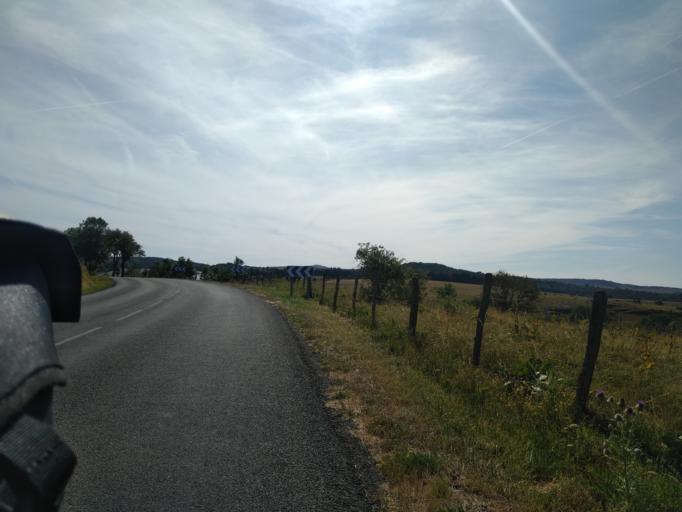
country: FR
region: Auvergne
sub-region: Departement du Cantal
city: Chaudes-Aigues
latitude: 44.6725
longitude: 3.0608
